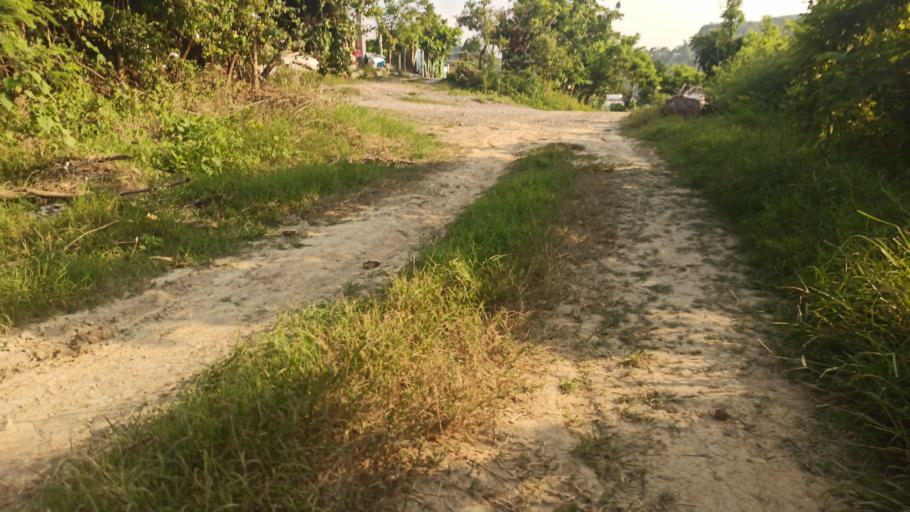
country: MX
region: Veracruz
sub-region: Papantla
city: Polutla
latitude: 20.6022
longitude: -97.2598
